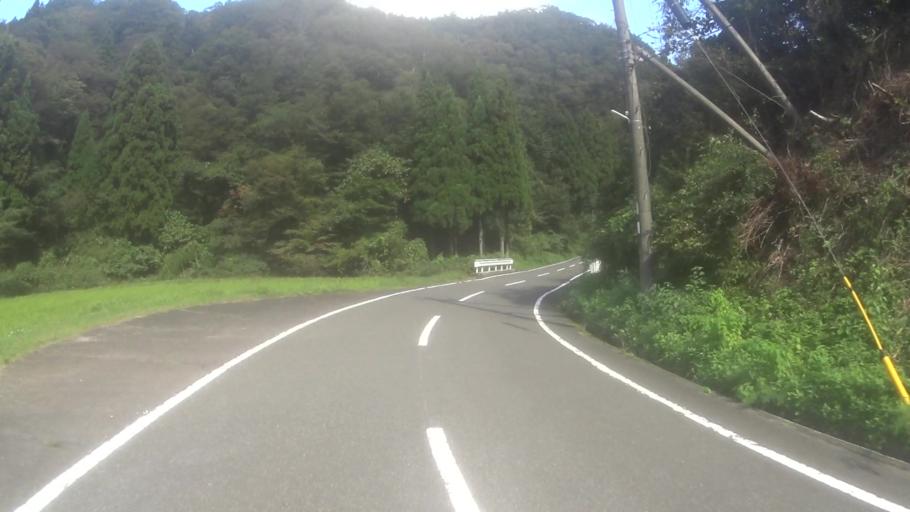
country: JP
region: Kyoto
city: Miyazu
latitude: 35.6773
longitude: 135.1547
